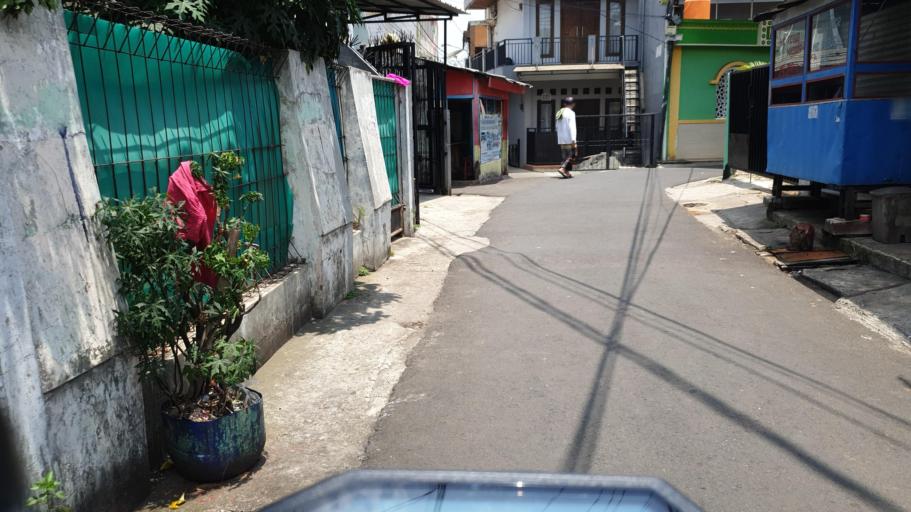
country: ID
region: West Java
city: Depok
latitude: -6.3291
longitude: 106.8325
